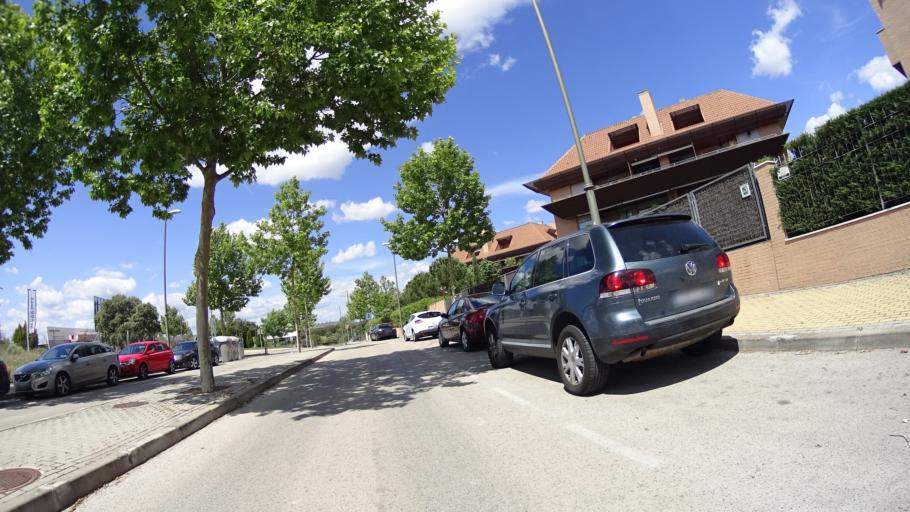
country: ES
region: Madrid
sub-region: Provincia de Madrid
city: Majadahonda
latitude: 40.4420
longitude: -3.8746
